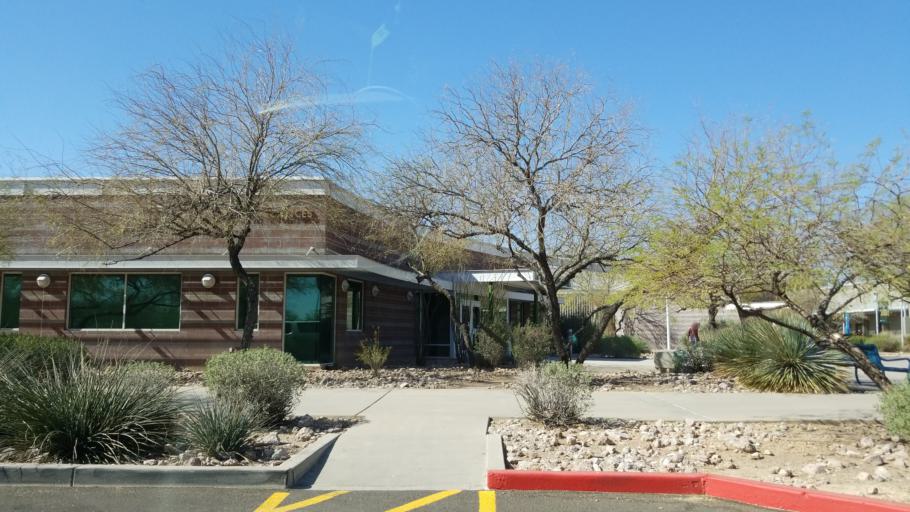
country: US
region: Arizona
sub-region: Maricopa County
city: Scottsdale
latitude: 33.5126
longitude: -111.8809
